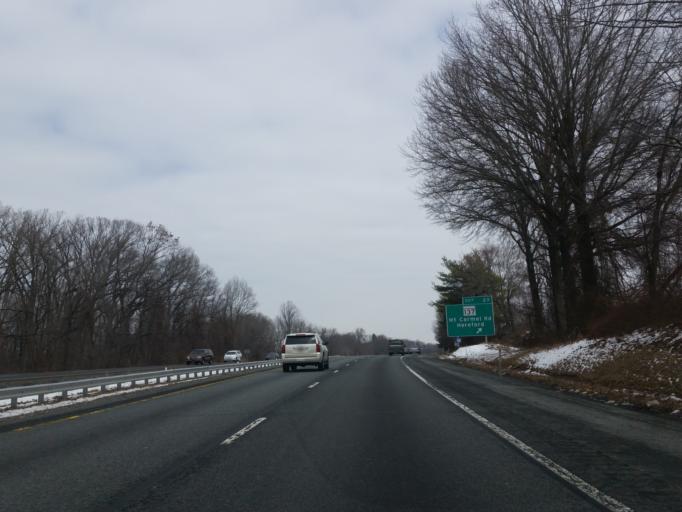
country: US
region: Maryland
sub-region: Baltimore County
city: Hunt Valley
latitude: 39.5844
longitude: -76.6769
